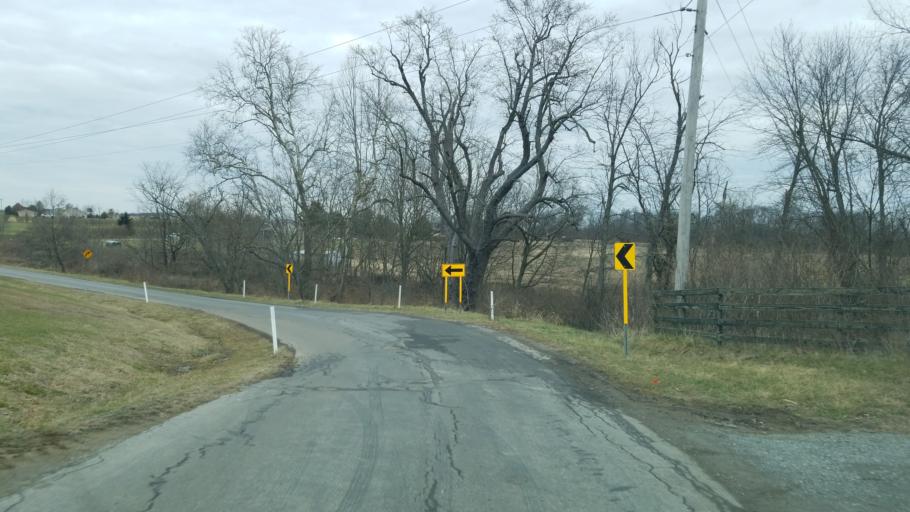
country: US
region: Ohio
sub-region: Highland County
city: Hillsboro
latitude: 39.2249
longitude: -83.4850
